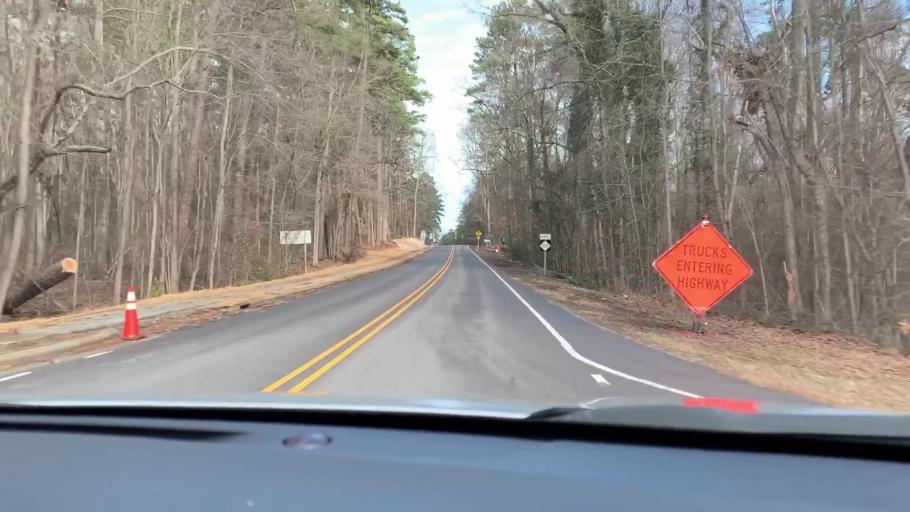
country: US
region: North Carolina
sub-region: Durham County
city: Durham
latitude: 35.9732
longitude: -78.9429
